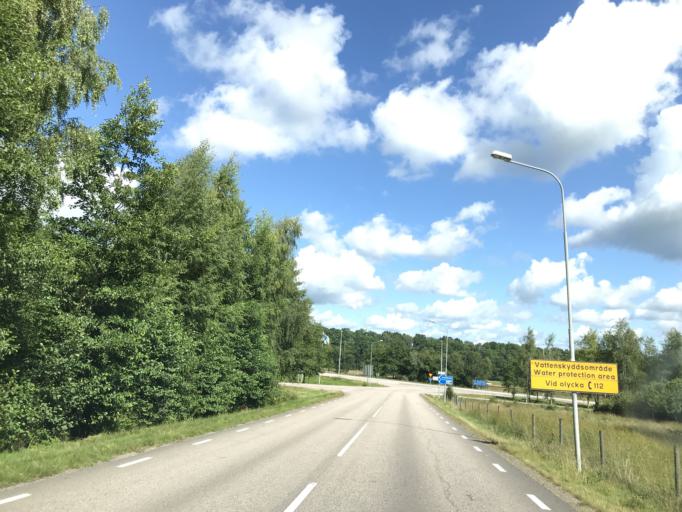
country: SE
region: Halland
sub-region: Laholms Kommun
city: Knared
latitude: 56.5114
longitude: 13.3215
